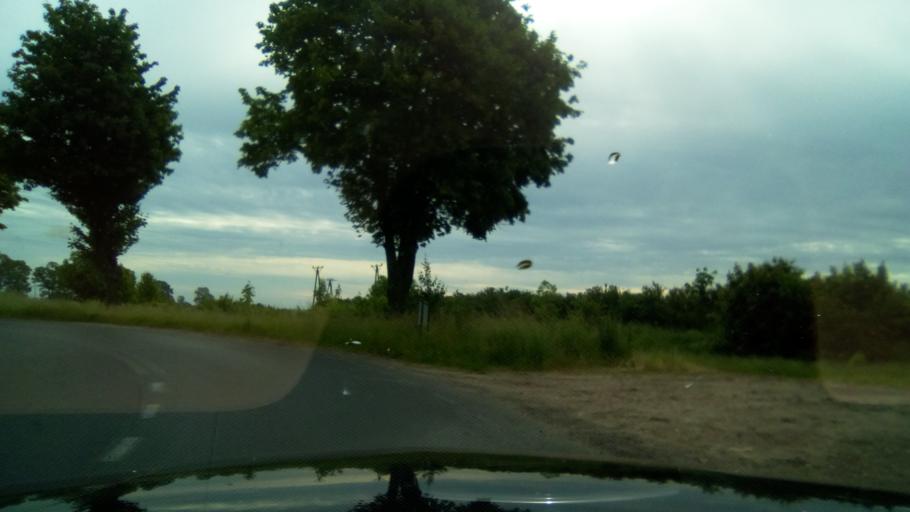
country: PL
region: Kujawsko-Pomorskie
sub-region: Powiat nakielski
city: Kcynia
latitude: 53.0008
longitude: 17.5054
